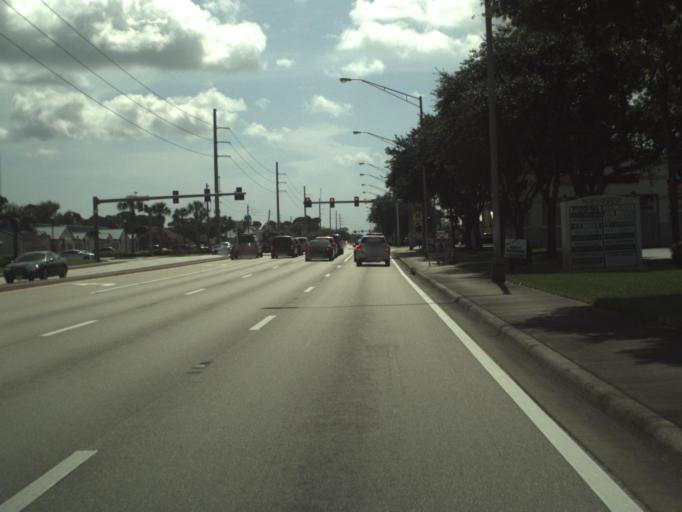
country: US
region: Florida
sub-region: Saint Lucie County
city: Port Saint Lucie
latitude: 27.2710
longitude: -80.2987
